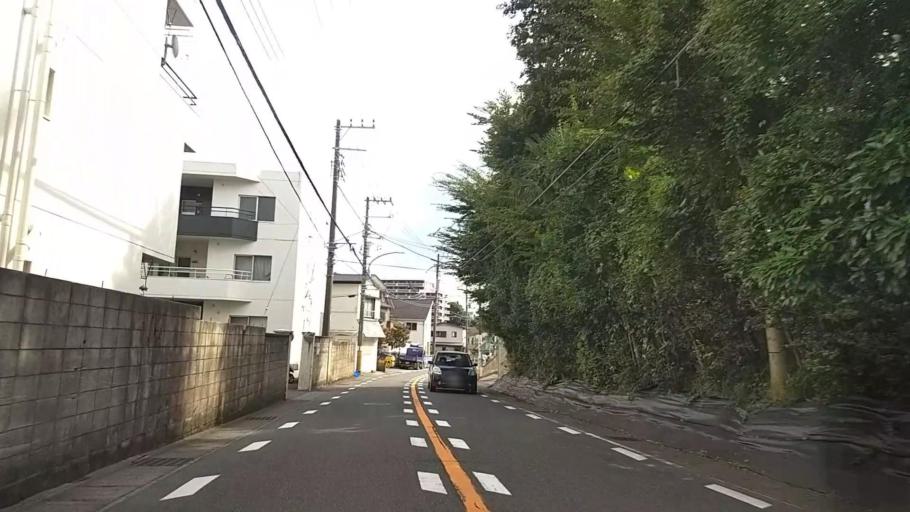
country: JP
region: Kanagawa
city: Yokohama
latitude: 35.4832
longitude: 139.5707
